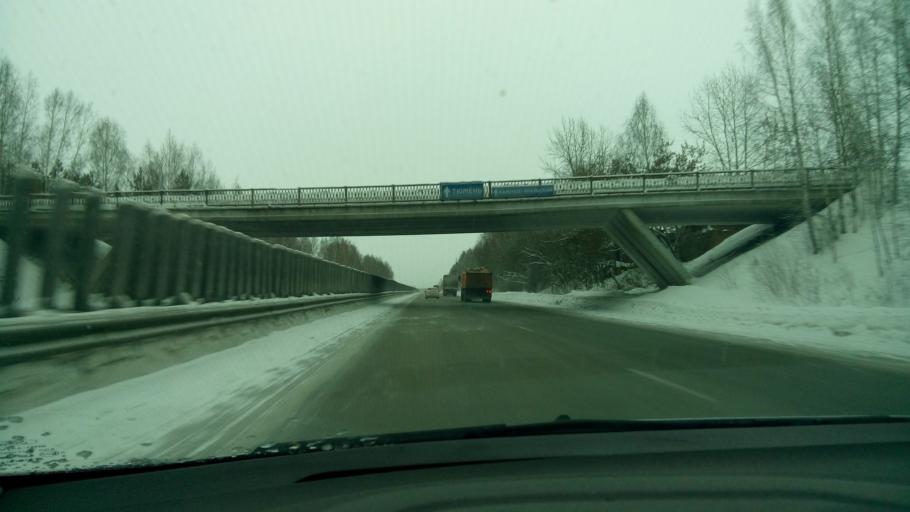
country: RU
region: Sverdlovsk
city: Aramil
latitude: 56.7738
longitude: 60.8720
